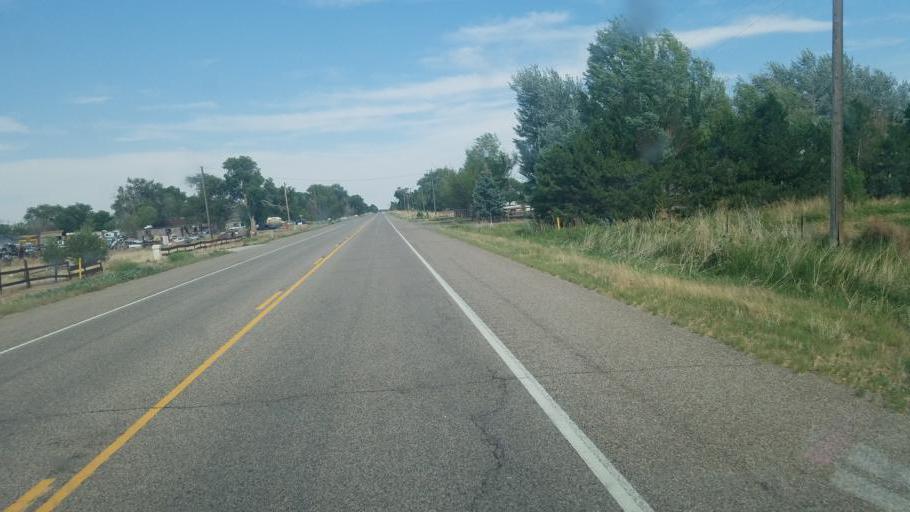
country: US
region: Colorado
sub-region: Otero County
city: Fowler
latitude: 38.2308
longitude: -104.3059
